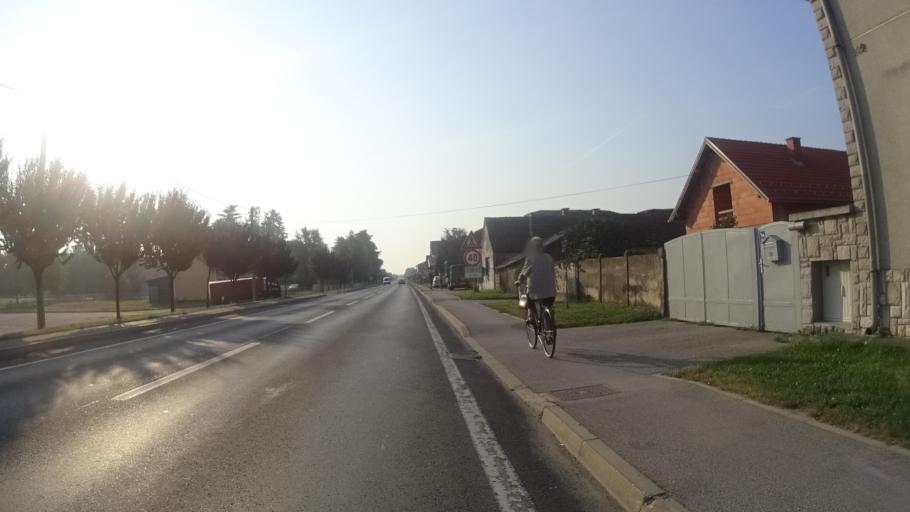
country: HR
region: Varazdinska
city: Sracinec
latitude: 46.3291
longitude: 16.2803
